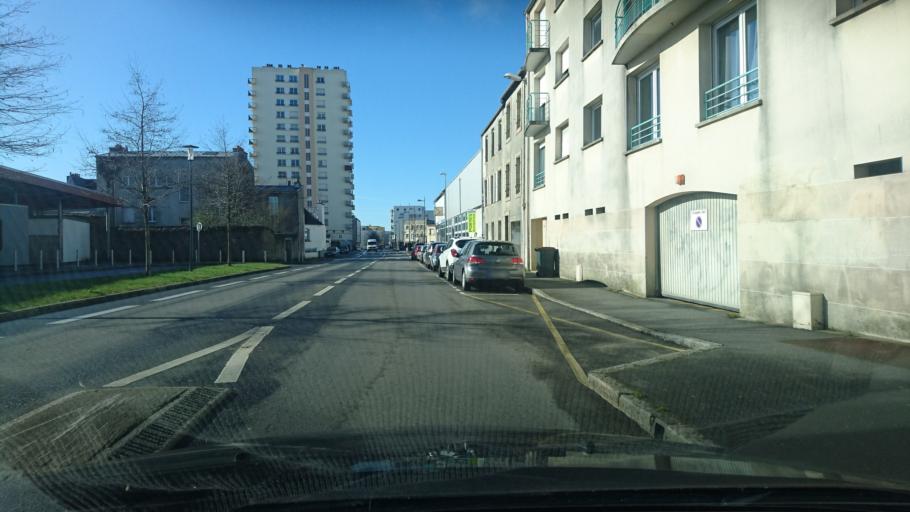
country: FR
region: Brittany
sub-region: Departement du Finistere
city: Brest
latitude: 48.3999
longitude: -4.4700
